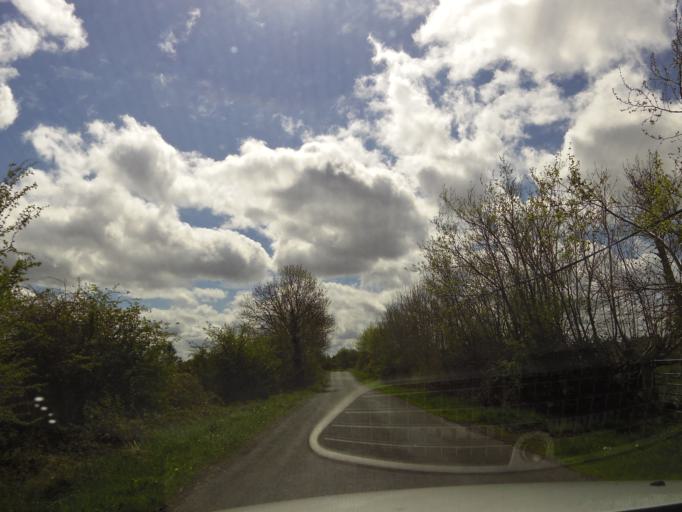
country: IE
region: Connaught
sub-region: Maigh Eo
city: Claremorris
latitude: 53.7792
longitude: -8.9609
